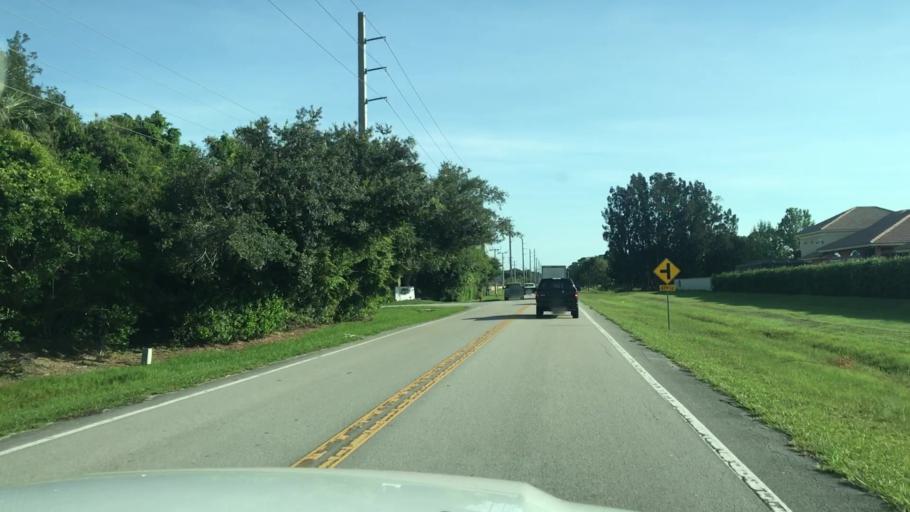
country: US
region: Florida
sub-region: Indian River County
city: Winter Beach
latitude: 27.7067
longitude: -80.4460
